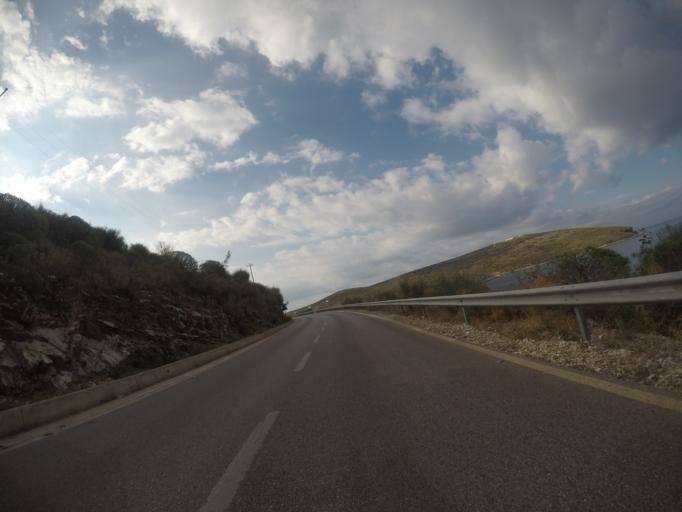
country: AL
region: Vlore
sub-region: Rrethi i Vlores
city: Himare
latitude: 40.0566
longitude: 19.8034
